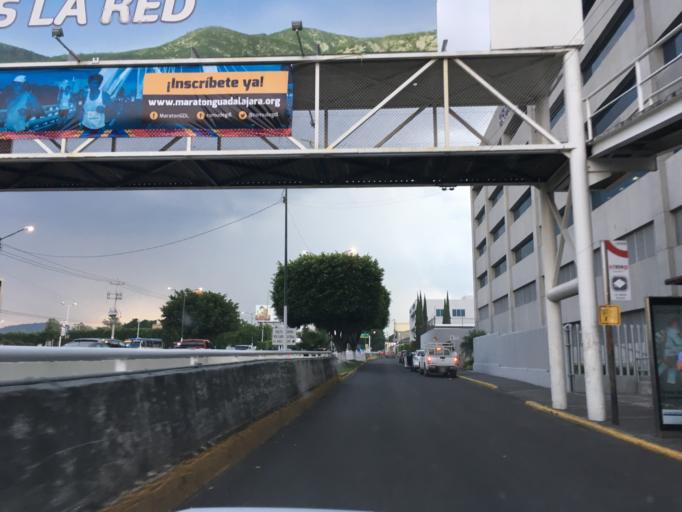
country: MX
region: Jalisco
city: Guadalajara
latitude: 20.6752
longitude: -103.4036
